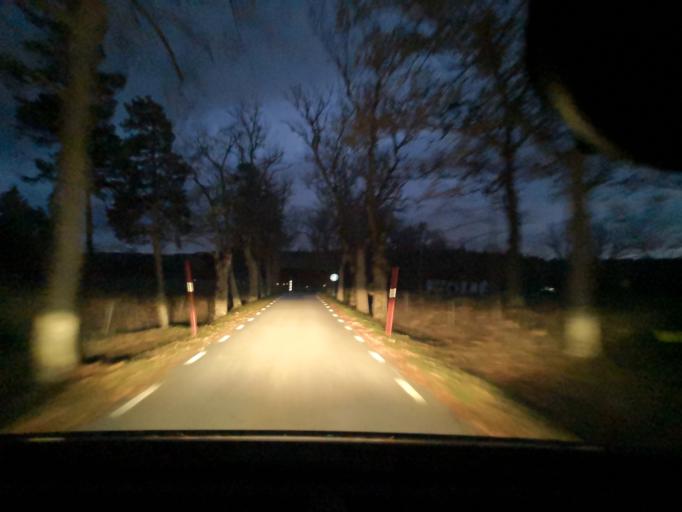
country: SE
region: Uppsala
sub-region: Enkopings Kommun
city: Hummelsta
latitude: 59.5356
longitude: 16.8606
